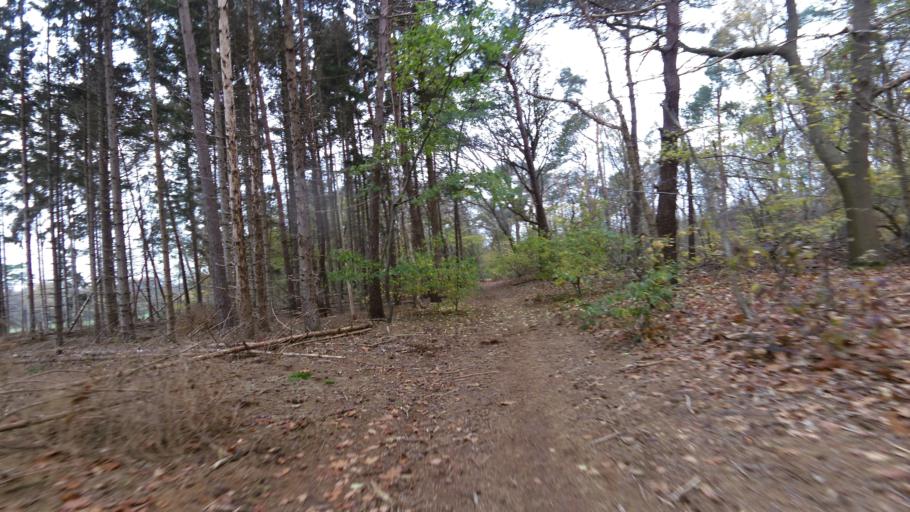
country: NL
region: North Holland
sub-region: Gemeente Hilversum
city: Hilversum
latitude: 52.2079
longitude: 5.2082
